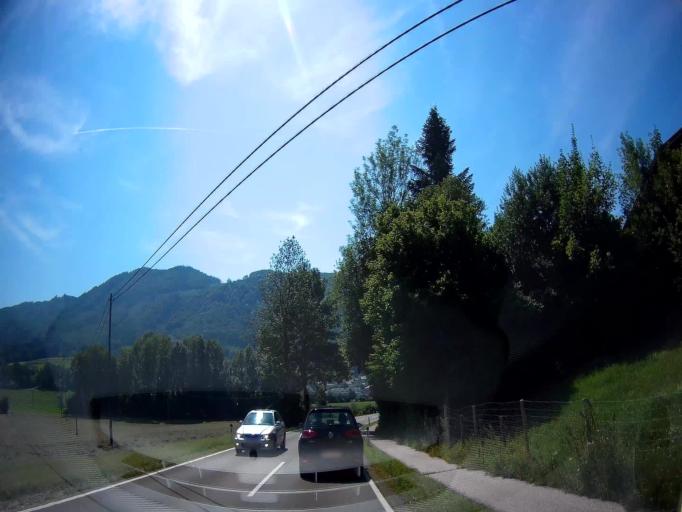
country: AT
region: Salzburg
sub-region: Politischer Bezirk Salzburg-Umgebung
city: Hallwang
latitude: 47.8376
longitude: 13.0801
